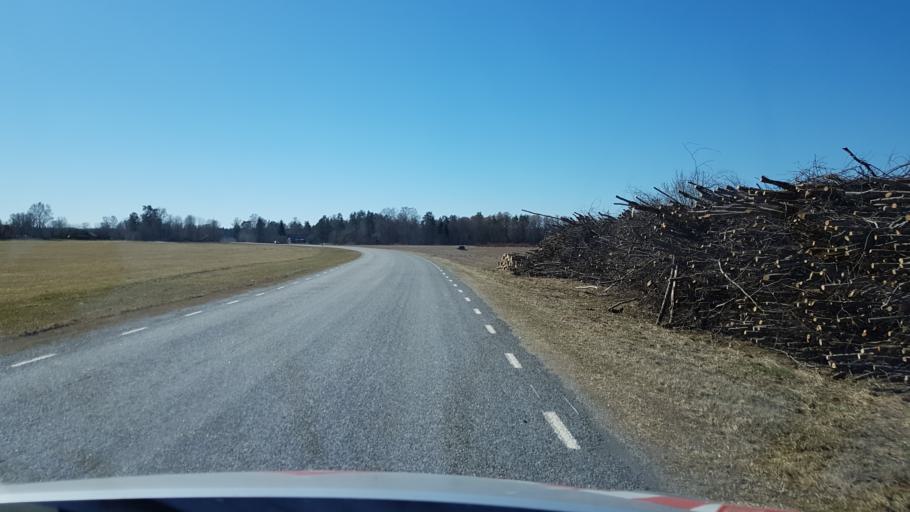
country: EE
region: Laeaene-Virumaa
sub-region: Haljala vald
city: Haljala
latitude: 59.4712
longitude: 26.2441
